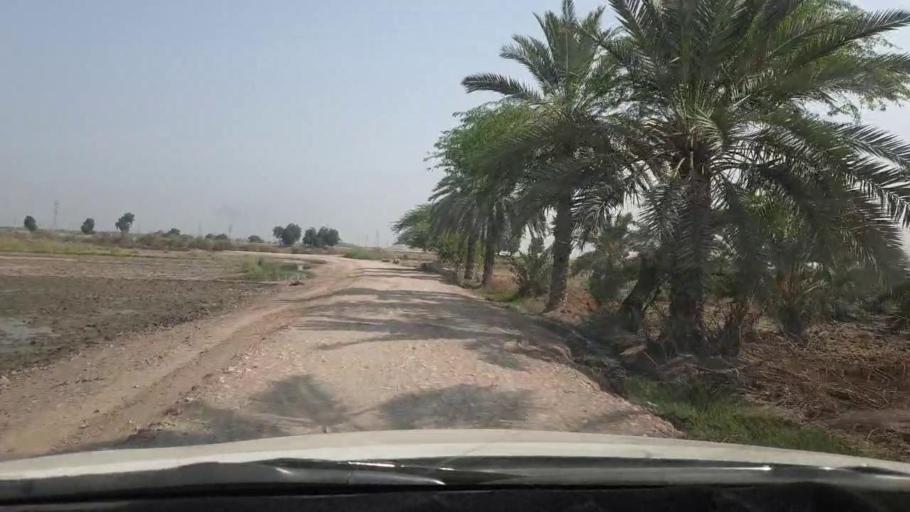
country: PK
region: Sindh
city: Rohri
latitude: 27.6335
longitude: 68.8852
